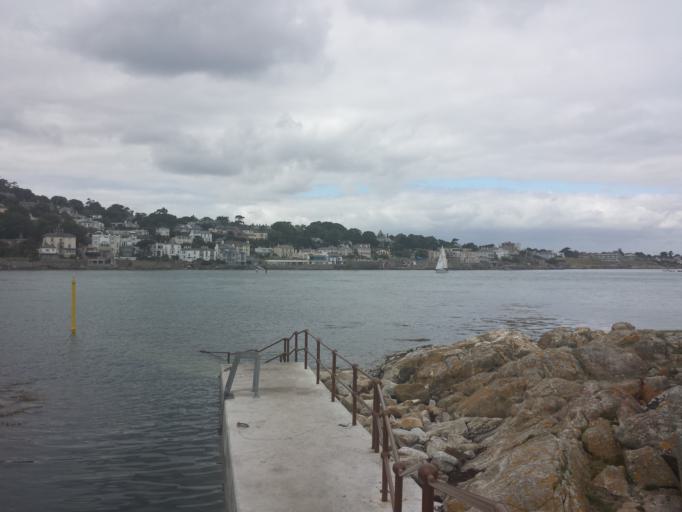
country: IE
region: Leinster
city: Dalkey
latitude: 53.2733
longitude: -6.0867
